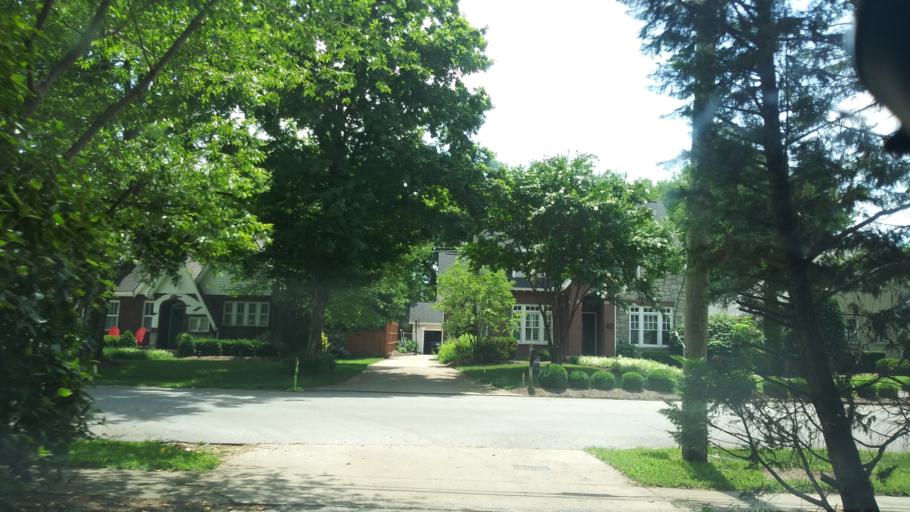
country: US
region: Tennessee
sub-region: Davidson County
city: Belle Meade
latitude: 36.1372
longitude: -86.8344
